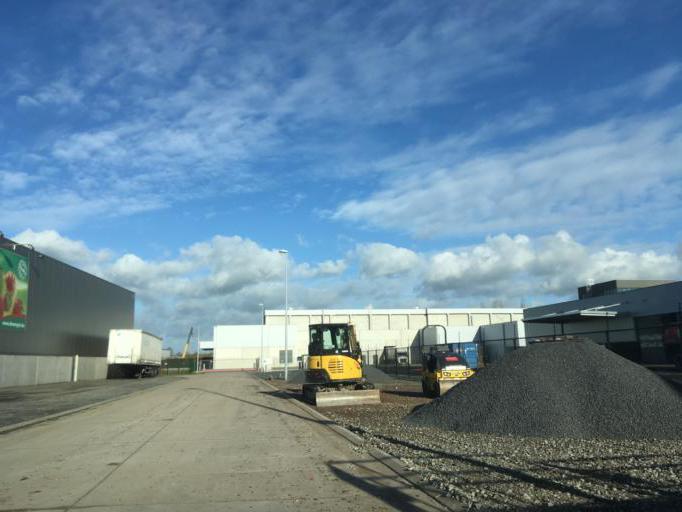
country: BE
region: Flanders
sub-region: Provincie West-Vlaanderen
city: Ardooie
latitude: 50.9686
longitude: 3.1755
